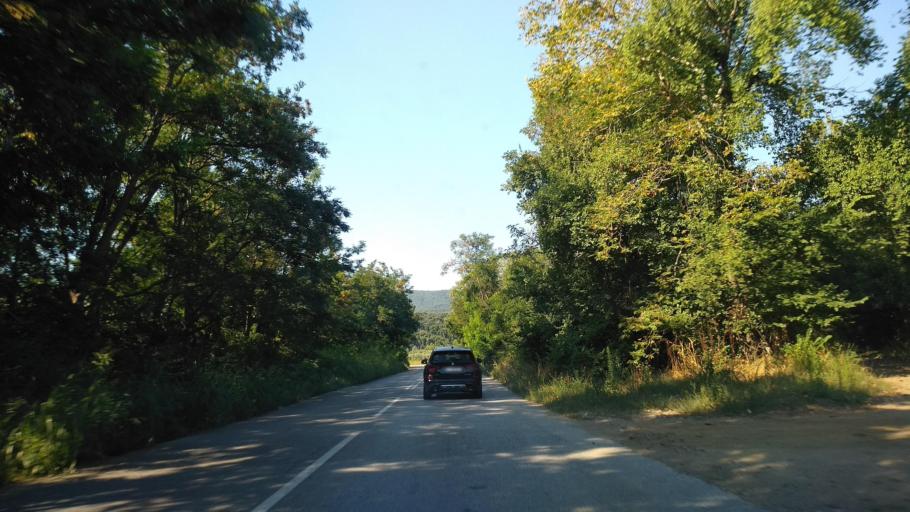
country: GR
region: Central Macedonia
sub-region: Nomos Chalkidikis
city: Stratonion
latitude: 40.4627
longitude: 23.8167
